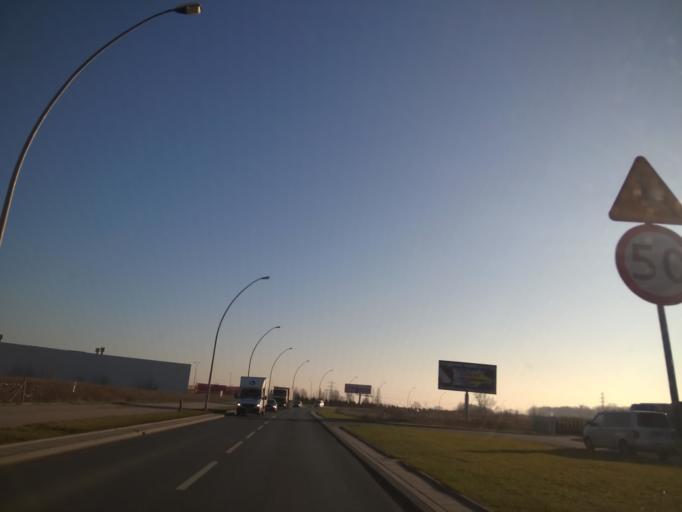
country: PL
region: Lower Silesian Voivodeship
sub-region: Powiat wroclawski
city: Bielany Wroclawskie
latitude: 51.0688
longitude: 16.9574
